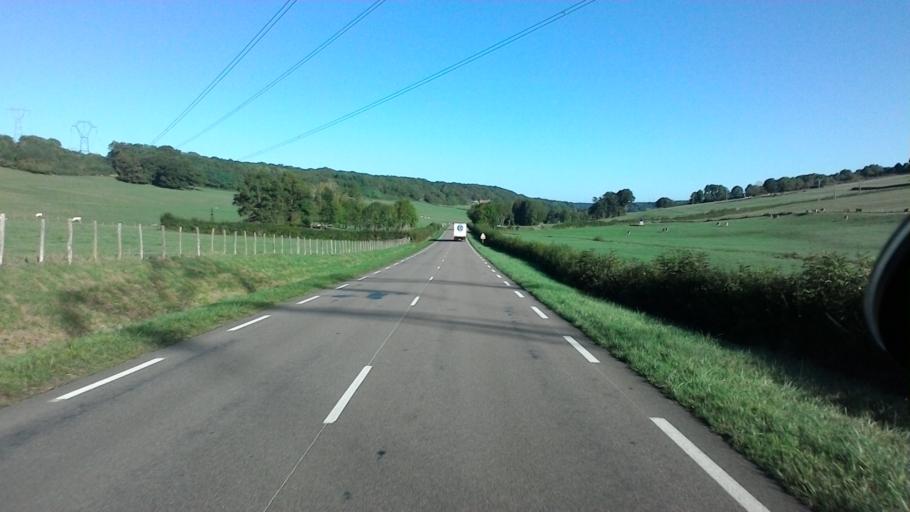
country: FR
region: Bourgogne
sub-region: Departement de la Cote-d'Or
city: Montbard
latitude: 47.5674
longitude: 4.3371
